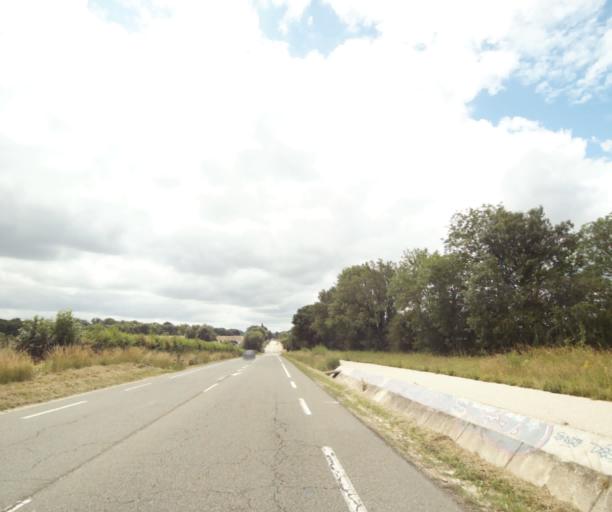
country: FR
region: Ile-de-France
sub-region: Departement des Yvelines
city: Bailly
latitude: 48.8214
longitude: 2.0820
